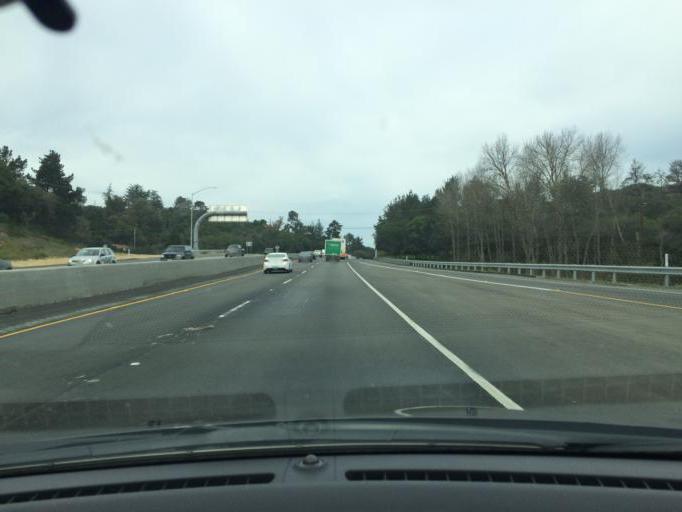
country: US
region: California
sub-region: Monterey County
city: Prunedale
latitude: 36.8203
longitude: -121.6306
